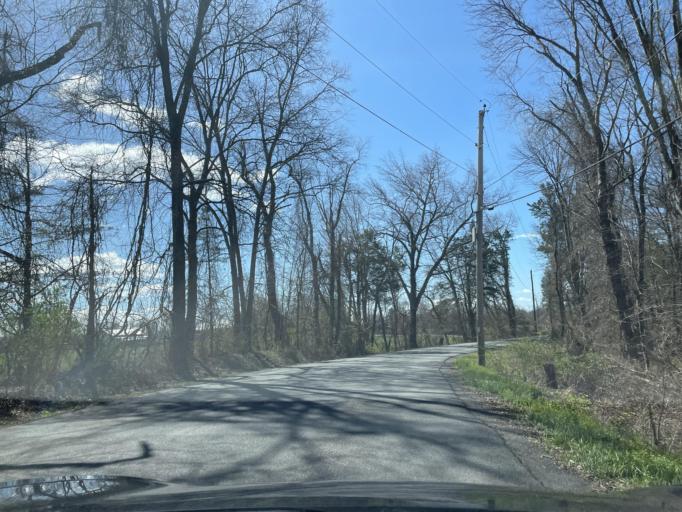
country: US
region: New York
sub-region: Ulster County
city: Saugerties South
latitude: 42.0485
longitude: -73.9935
